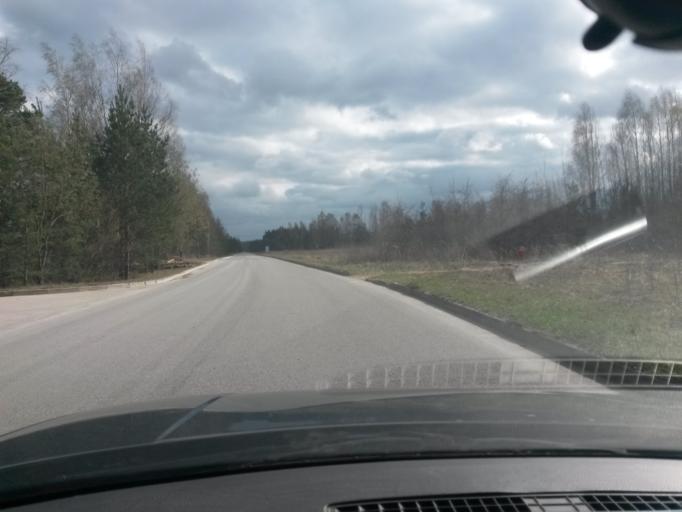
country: LV
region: Stopini
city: Ulbroka
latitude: 56.9050
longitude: 24.2465
